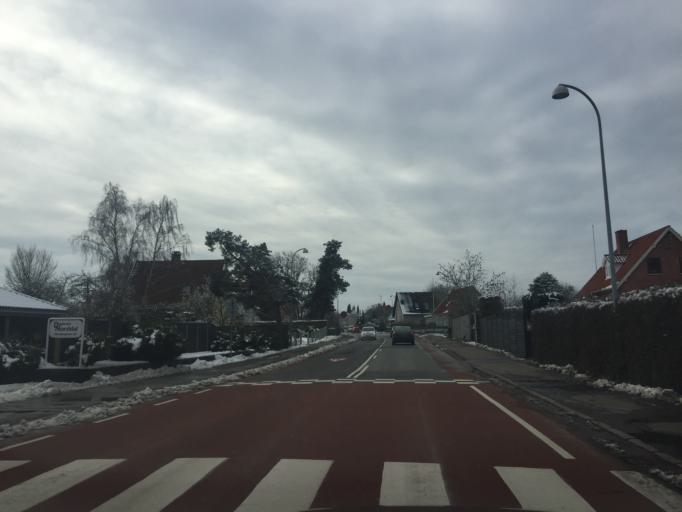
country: DK
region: Capital Region
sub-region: Gribskov Kommune
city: Helsinge
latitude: 56.0223
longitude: 12.1902
